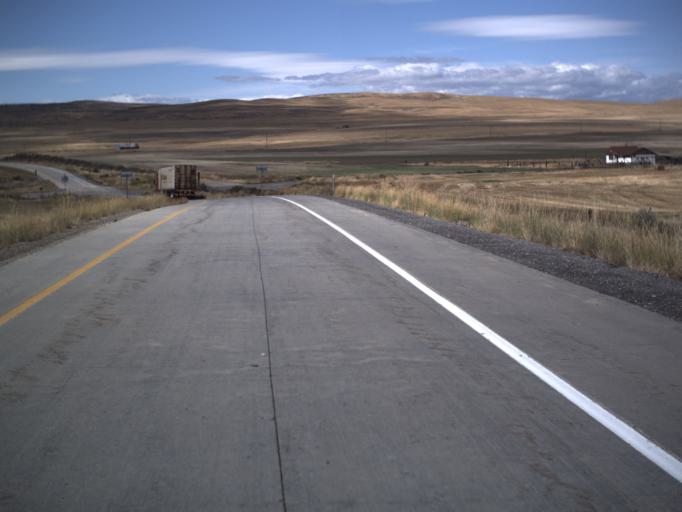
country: US
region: Utah
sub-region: Box Elder County
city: Garland
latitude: 41.8846
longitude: -112.4874
